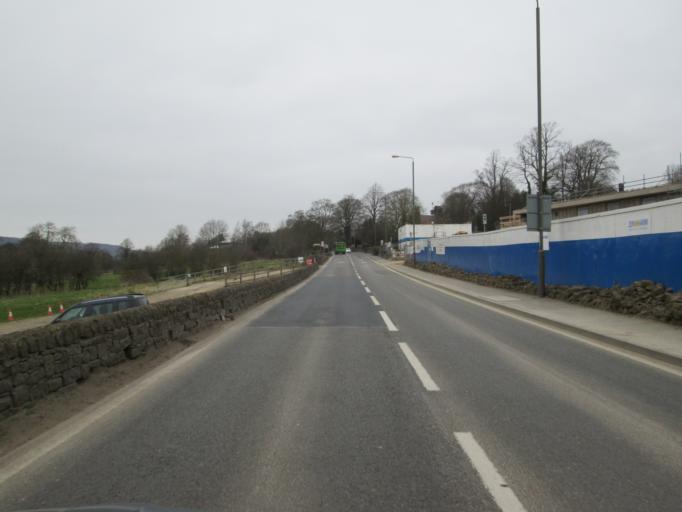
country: GB
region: England
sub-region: Derbyshire
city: Matlock
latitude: 53.1492
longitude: -1.5746
